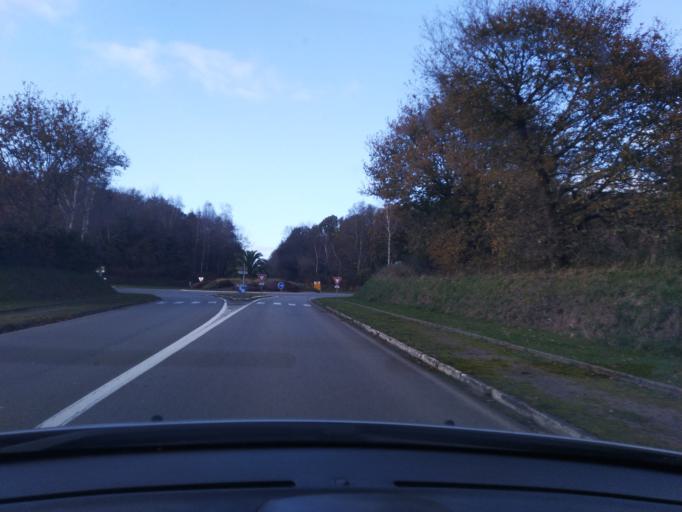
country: FR
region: Brittany
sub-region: Departement du Finistere
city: Morlaix
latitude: 48.5838
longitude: -3.8035
